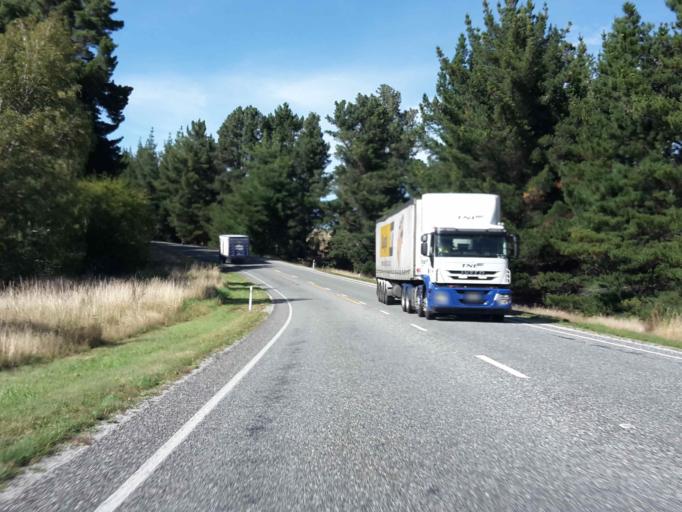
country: NZ
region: Otago
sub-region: Queenstown-Lakes District
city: Wanaka
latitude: -44.7046
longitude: 169.1968
